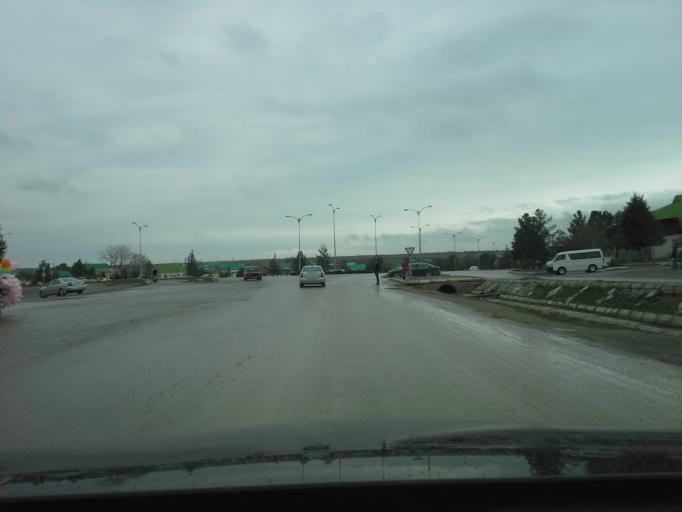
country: TM
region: Ahal
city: Abadan
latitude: 37.9649
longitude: 58.2205
